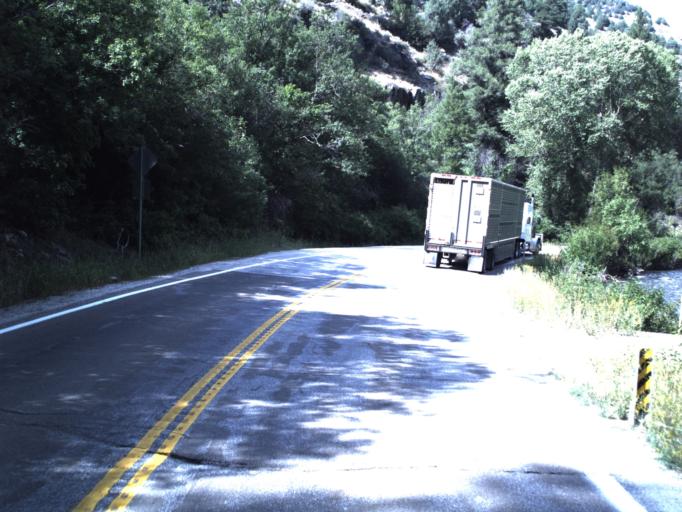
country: US
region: Utah
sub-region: Cache County
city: North Logan
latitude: 41.8147
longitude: -111.6187
